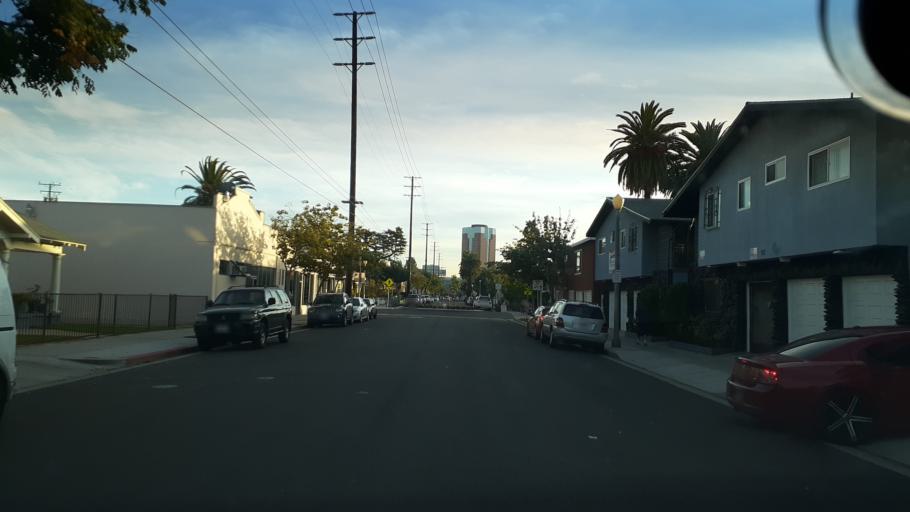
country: US
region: California
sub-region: Los Angeles County
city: Long Beach
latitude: 33.7785
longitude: -118.1994
